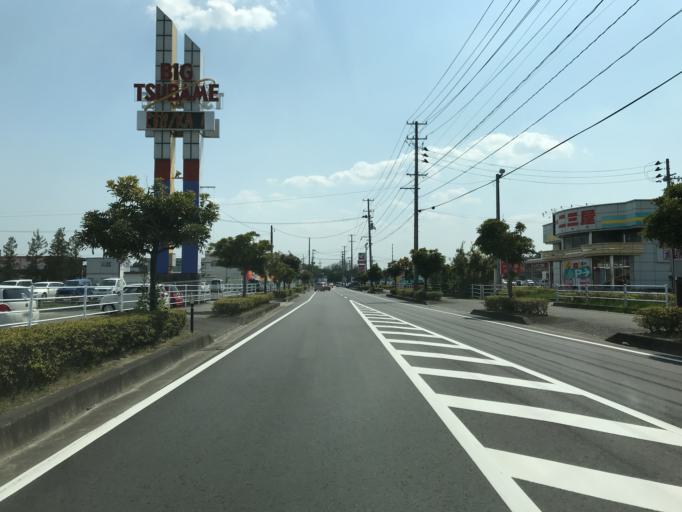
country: JP
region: Ibaraki
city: Kitaibaraki
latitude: 36.9093
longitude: 140.7733
